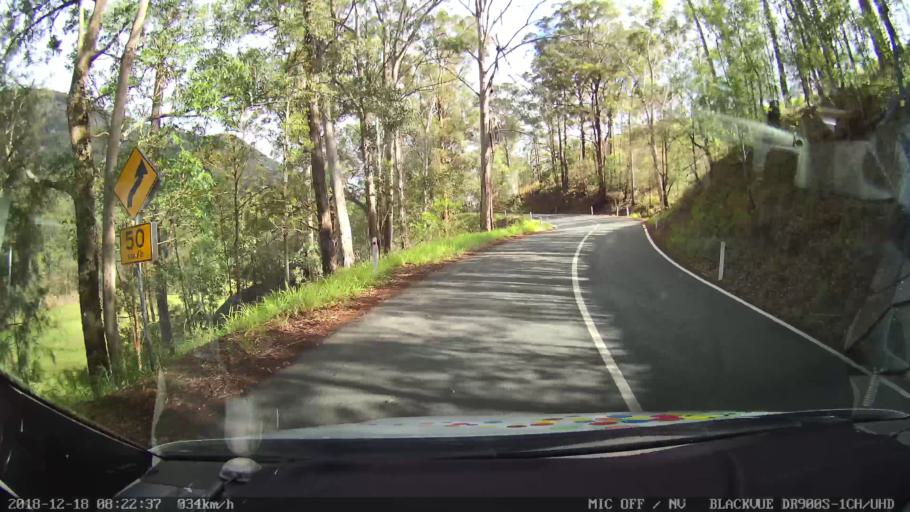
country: AU
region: New South Wales
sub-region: Kyogle
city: Kyogle
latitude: -28.3244
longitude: 152.7254
